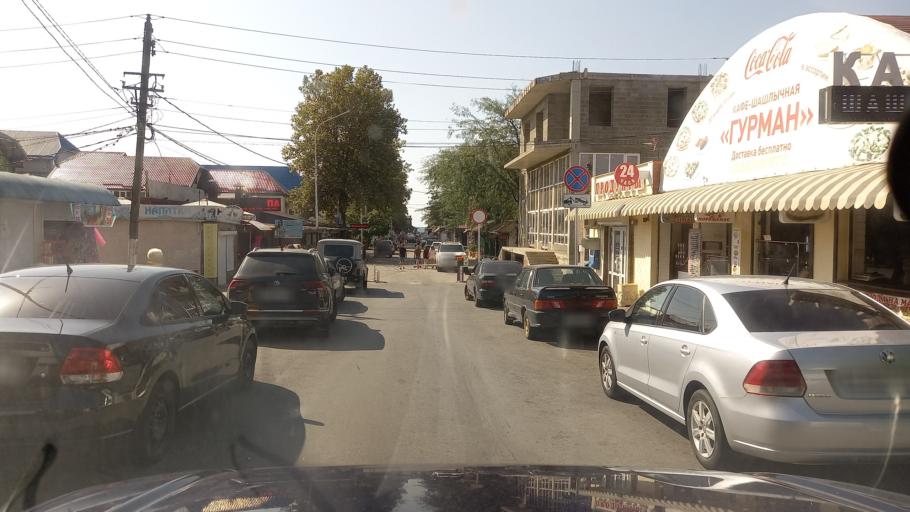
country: RU
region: Krasnodarskiy
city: Arkhipo-Osipovka
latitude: 44.3609
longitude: 38.5322
